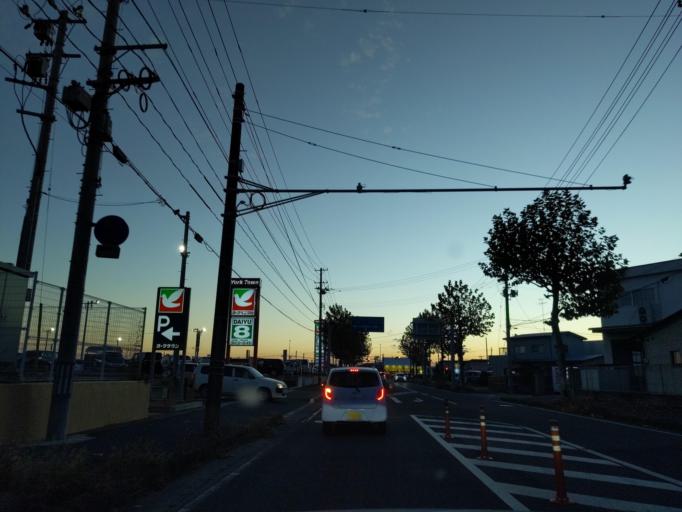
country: JP
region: Fukushima
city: Koriyama
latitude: 37.3671
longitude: 140.3939
